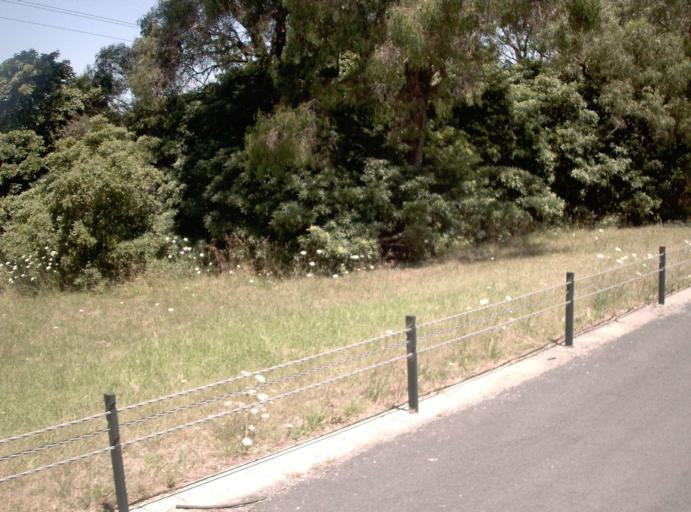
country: AU
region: Victoria
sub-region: Cardinia
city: Garfield
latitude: -38.0683
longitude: 145.5953
